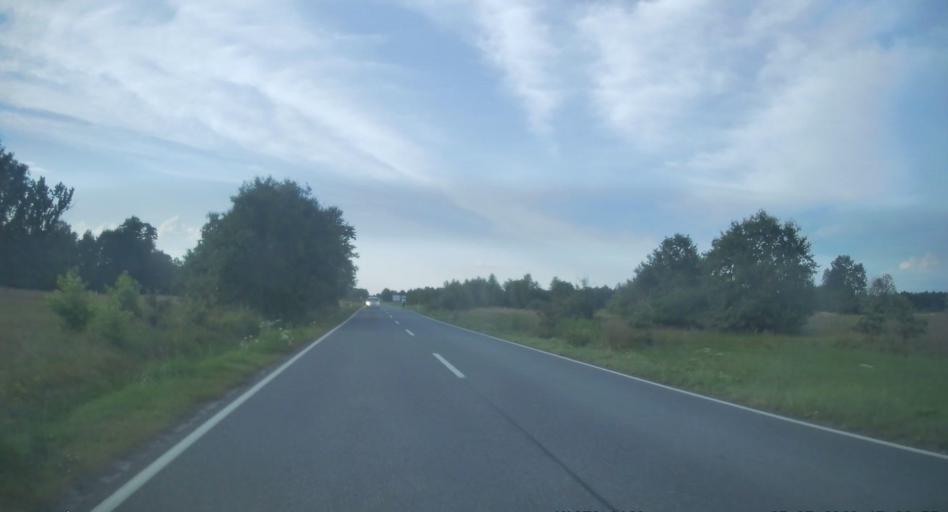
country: PL
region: Lesser Poland Voivodeship
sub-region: Powiat brzeski
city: Szczurowa
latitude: 50.0727
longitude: 20.6347
